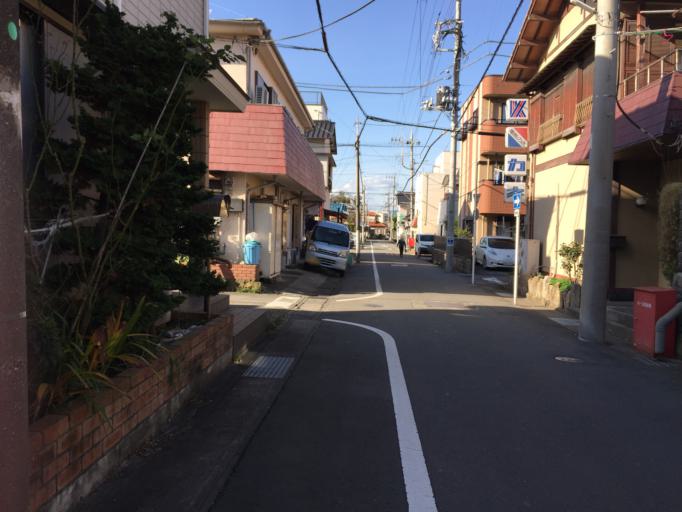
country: JP
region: Shizuoka
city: Numazu
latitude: 35.0774
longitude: 138.8600
